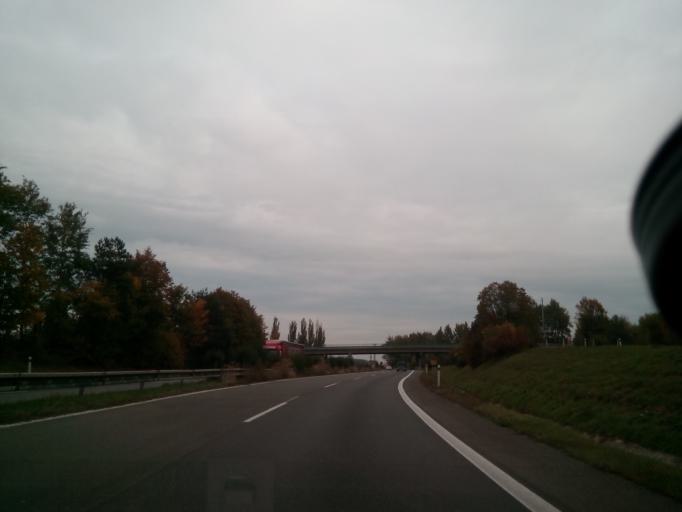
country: SK
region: Presovsky
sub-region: Okres Presov
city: Presov
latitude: 48.9509
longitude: 21.2556
